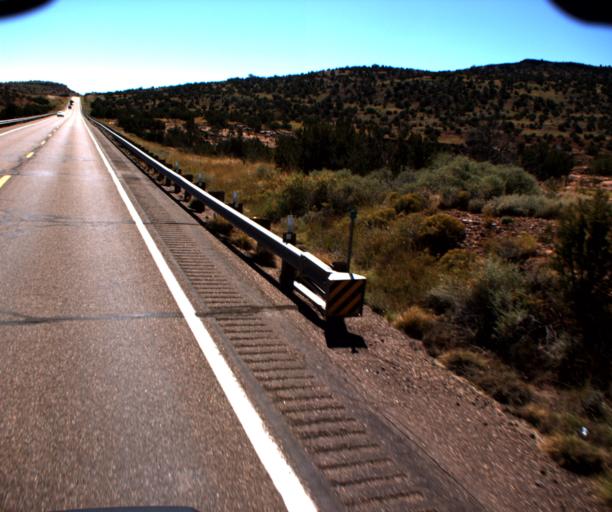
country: US
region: Arizona
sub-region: Apache County
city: Saint Johns
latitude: 34.3680
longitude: -109.3923
